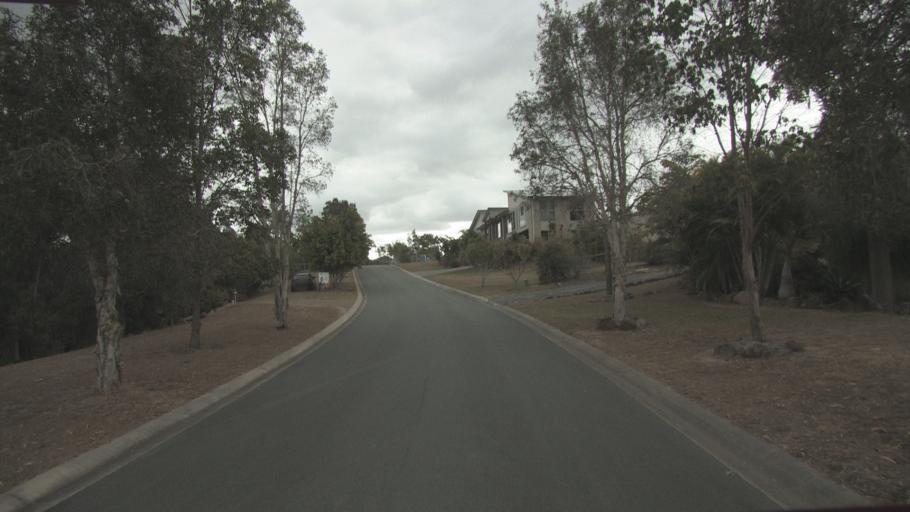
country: AU
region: Queensland
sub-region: Logan
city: Cedar Vale
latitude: -27.8717
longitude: 153.0730
